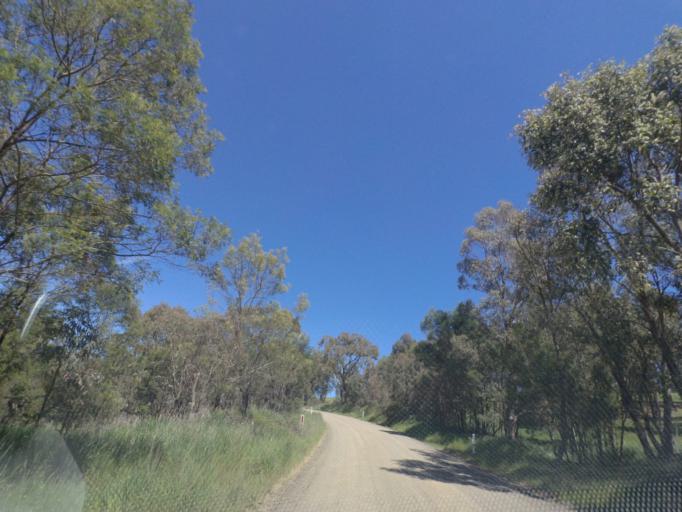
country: AU
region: Victoria
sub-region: Whittlesea
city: Whittlesea
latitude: -37.2821
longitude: 145.0096
